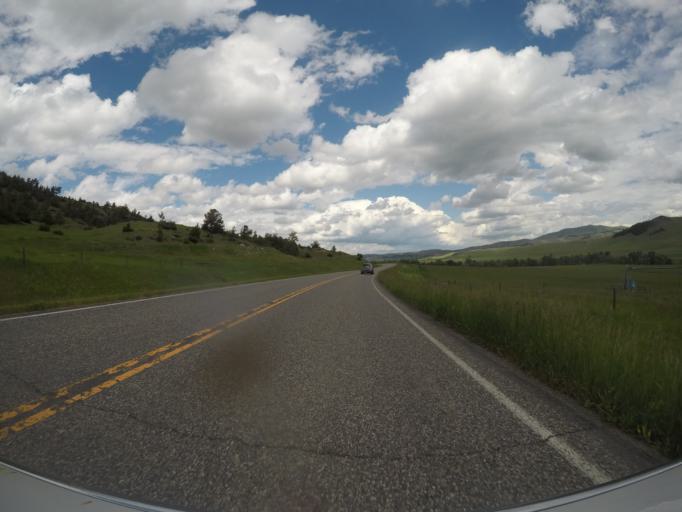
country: US
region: Montana
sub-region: Sweet Grass County
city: Big Timber
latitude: 45.6881
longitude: -110.0744
